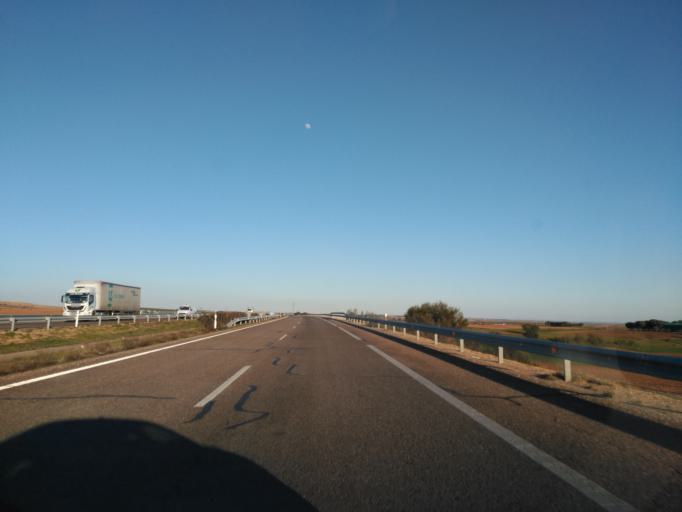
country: ES
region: Castille and Leon
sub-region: Provincia de Salamanca
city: Parada de Rubiales
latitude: 41.1629
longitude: -5.4270
